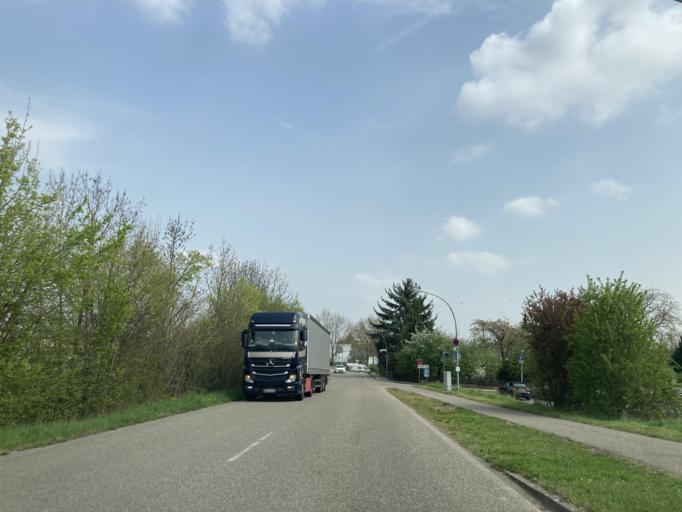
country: DE
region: Baden-Wuerttemberg
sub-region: Karlsruhe Region
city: Kronau
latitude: 49.2204
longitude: 8.6441
